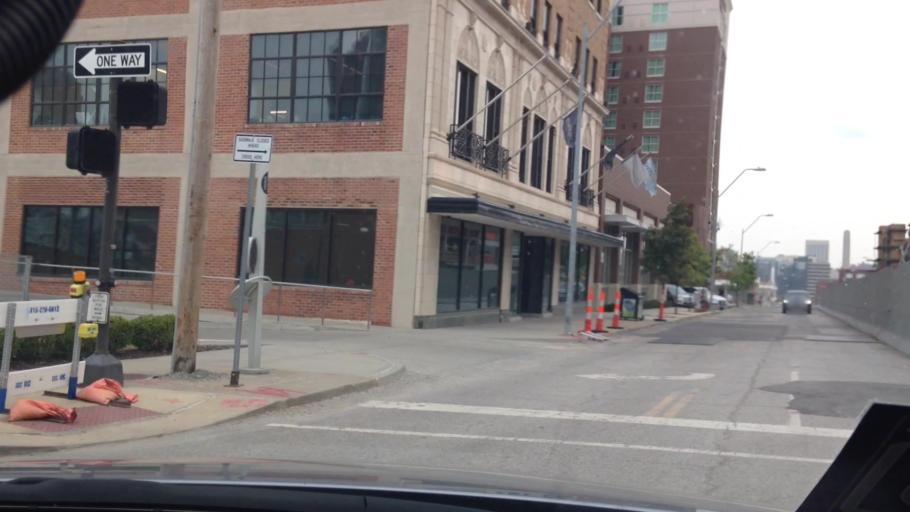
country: US
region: Missouri
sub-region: Jackson County
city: Kansas City
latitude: 39.0958
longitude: -94.5845
